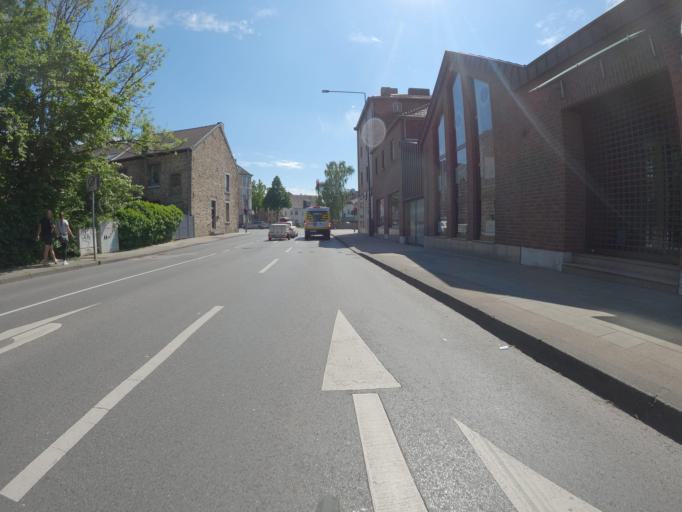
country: DE
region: North Rhine-Westphalia
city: Stolberg
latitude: 50.7519
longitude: 6.1599
